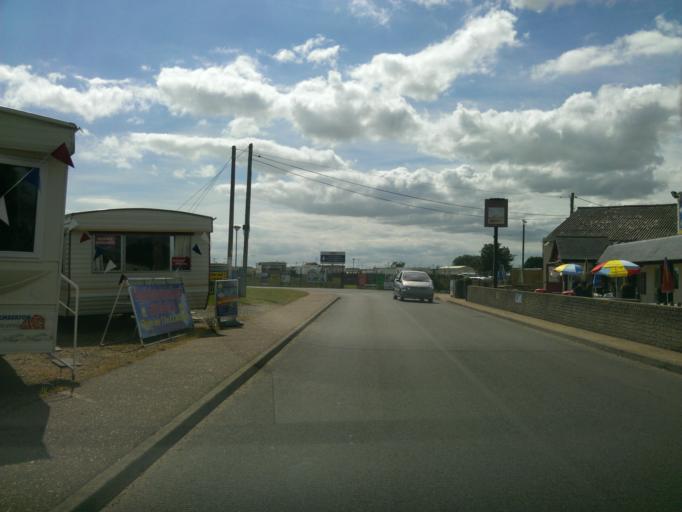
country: GB
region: England
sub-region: Essex
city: Saint Osyth
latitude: 51.7771
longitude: 1.0869
